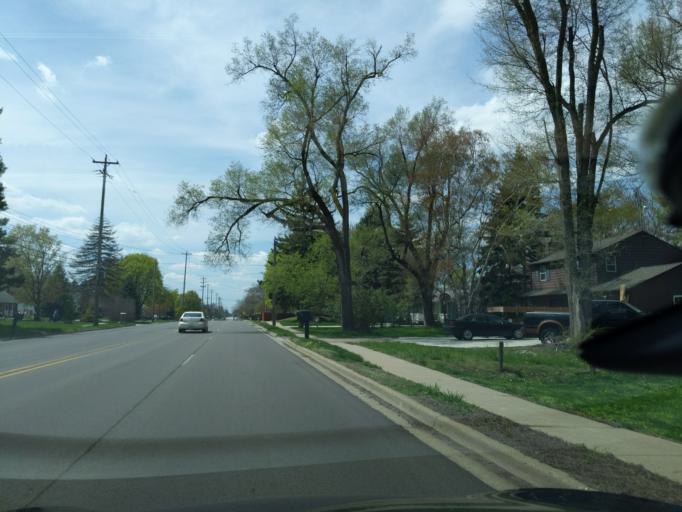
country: US
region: Michigan
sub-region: Eaton County
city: Waverly
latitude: 42.7266
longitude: -84.6146
